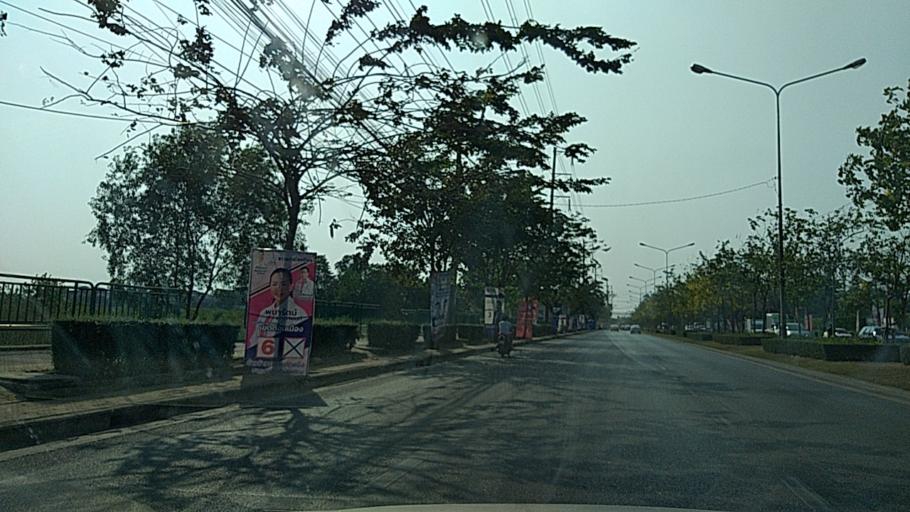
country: TH
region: Bangkok
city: Don Mueang
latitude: 13.9317
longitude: 100.5712
